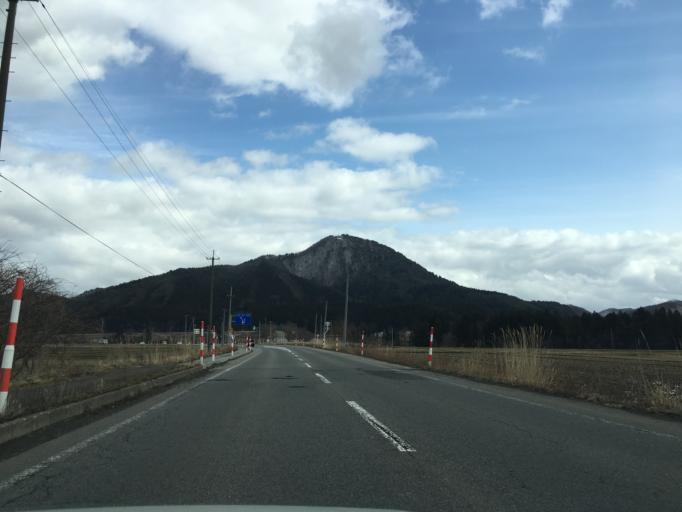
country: JP
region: Akita
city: Hanawa
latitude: 40.2221
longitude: 140.6713
